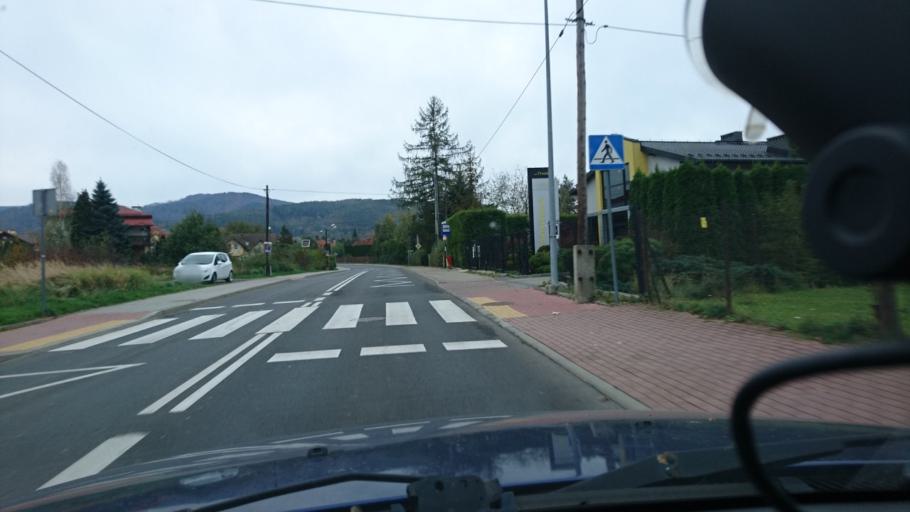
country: PL
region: Silesian Voivodeship
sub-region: Bielsko-Biala
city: Bielsko-Biala
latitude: 49.8006
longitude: 19.0220
